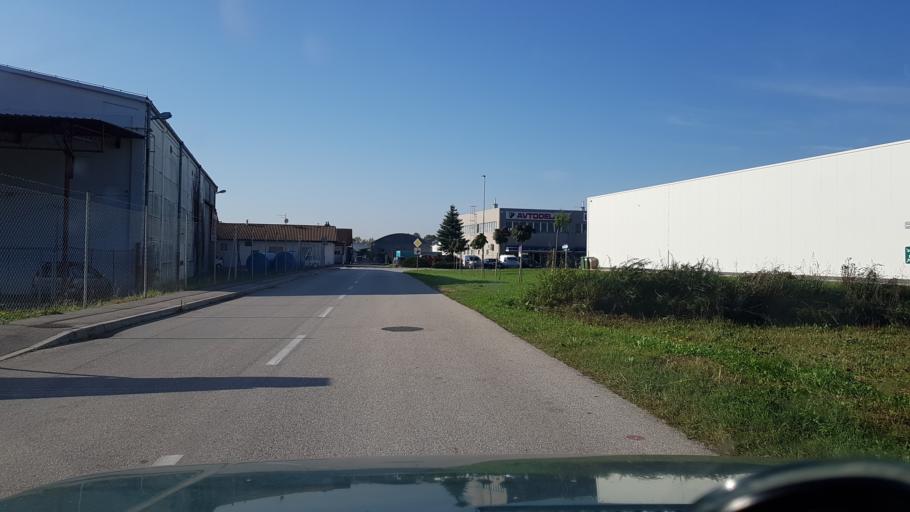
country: SI
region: Sempeter-Vrtojba
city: Sempeter pri Gorici
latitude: 45.9263
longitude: 13.6331
